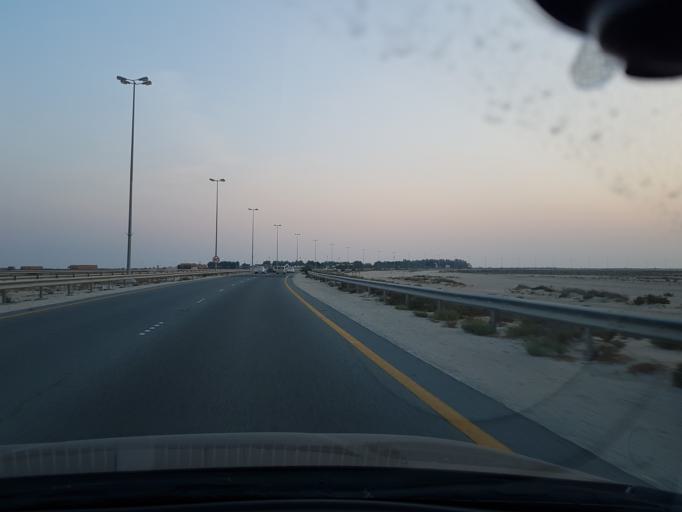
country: BH
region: Central Governorate
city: Dar Kulayb
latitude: 25.9972
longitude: 50.4842
